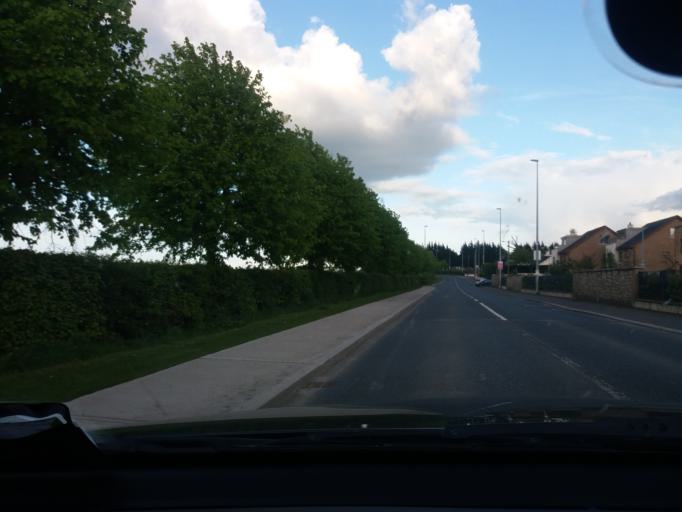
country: IE
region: Leinster
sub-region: South Dublin
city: Newcastle
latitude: 53.2955
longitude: -6.4907
